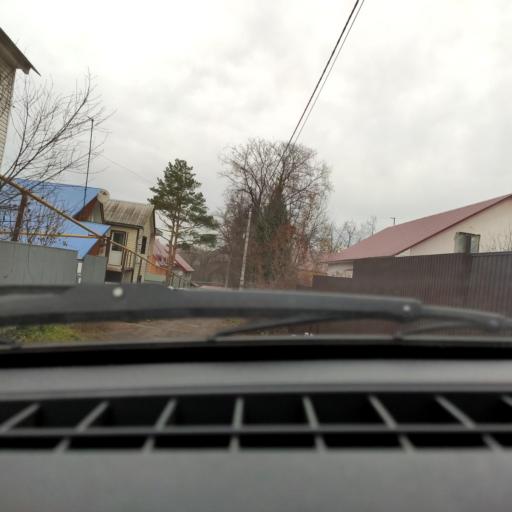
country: RU
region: Bashkortostan
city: Ufa
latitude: 54.8299
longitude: 56.0731
